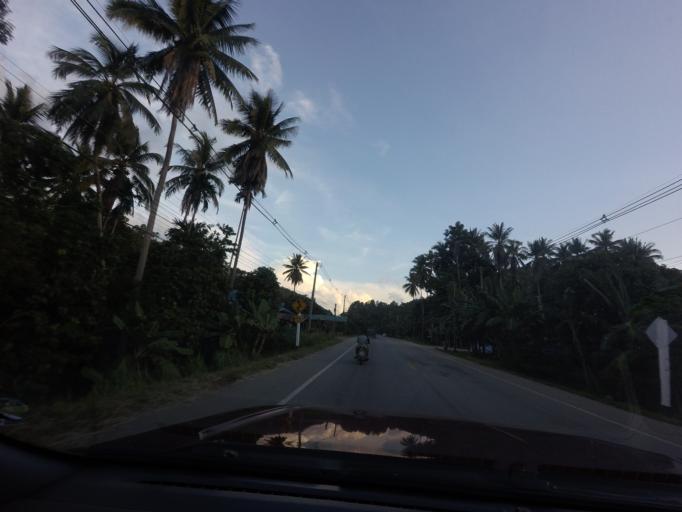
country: TH
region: Yala
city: Than To
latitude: 6.1007
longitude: 101.1813
